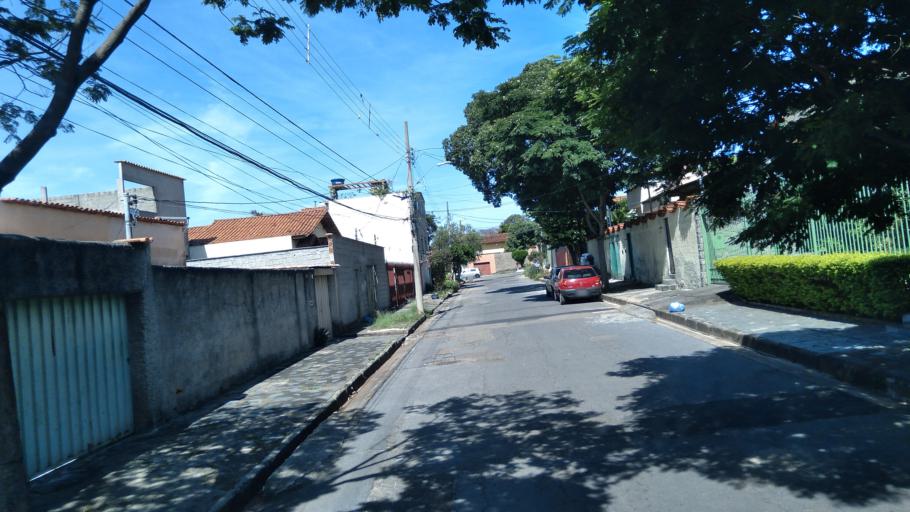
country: BR
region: Minas Gerais
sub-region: Contagem
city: Contagem
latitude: -19.8924
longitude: -44.0122
